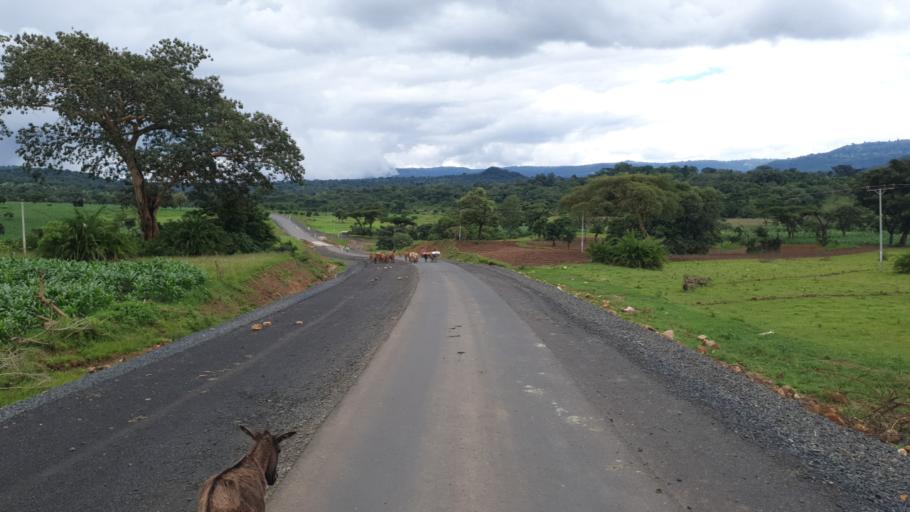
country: ET
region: Oromiya
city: Shambu
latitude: 10.0863
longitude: 36.8948
